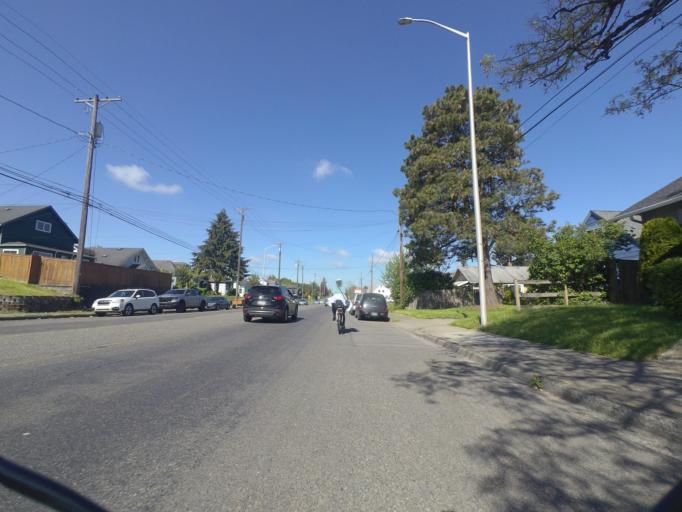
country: US
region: Washington
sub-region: Pierce County
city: Tacoma
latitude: 47.2065
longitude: -122.4529
